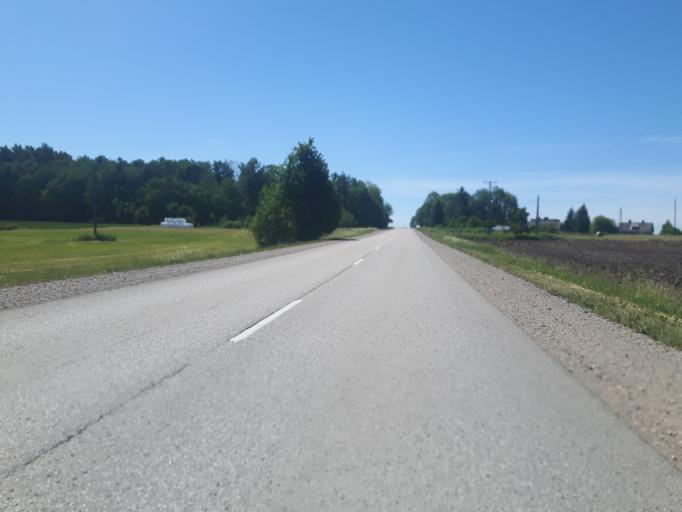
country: LV
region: Durbe
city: Liegi
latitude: 56.5903
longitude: 21.2725
